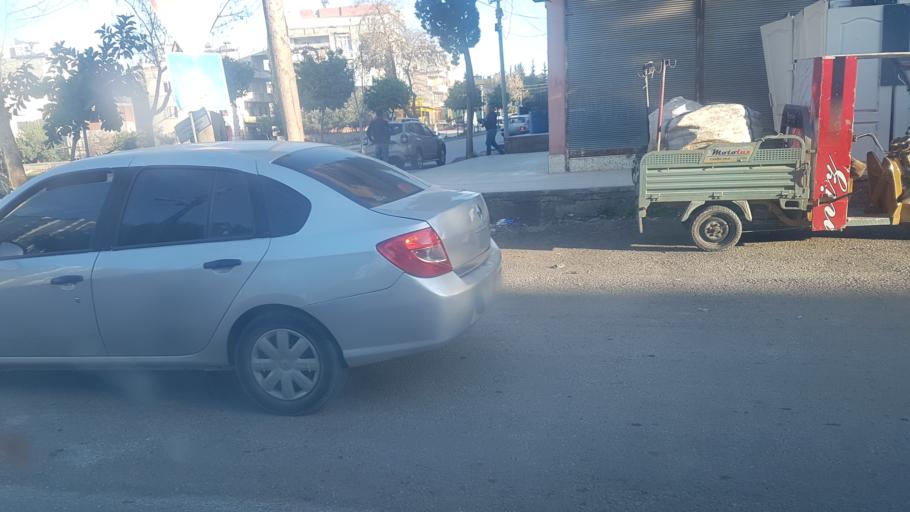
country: TR
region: Adana
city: Seyhan
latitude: 37.0229
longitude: 35.2711
